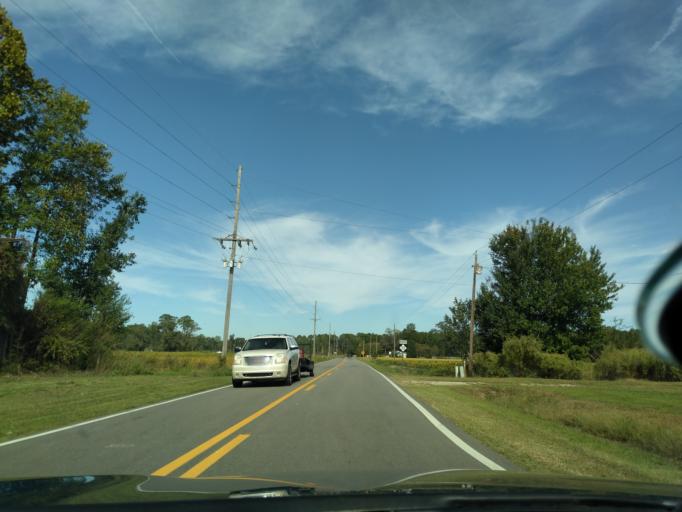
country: US
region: North Carolina
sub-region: Beaufort County
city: River Road
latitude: 35.5135
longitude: -76.9640
